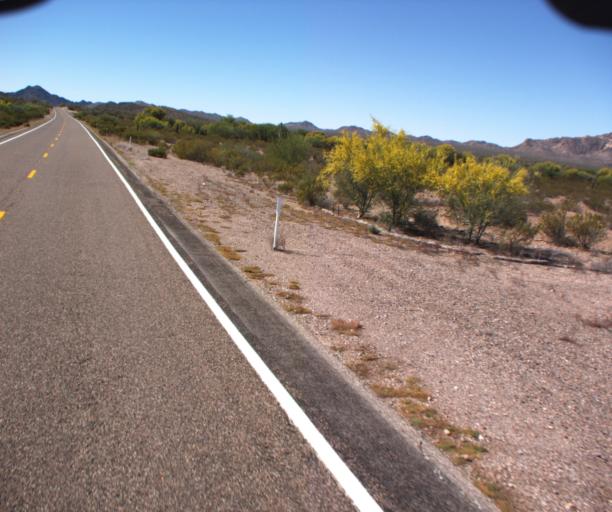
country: MX
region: Sonora
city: Sonoyta
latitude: 32.0257
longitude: -112.8012
